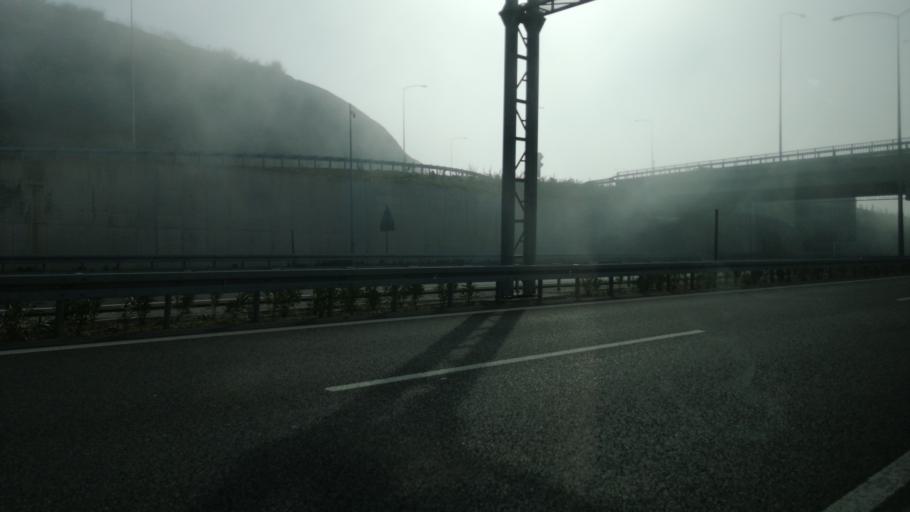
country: TR
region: Kocaeli
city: Tavsanli
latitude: 40.7771
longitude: 29.5181
